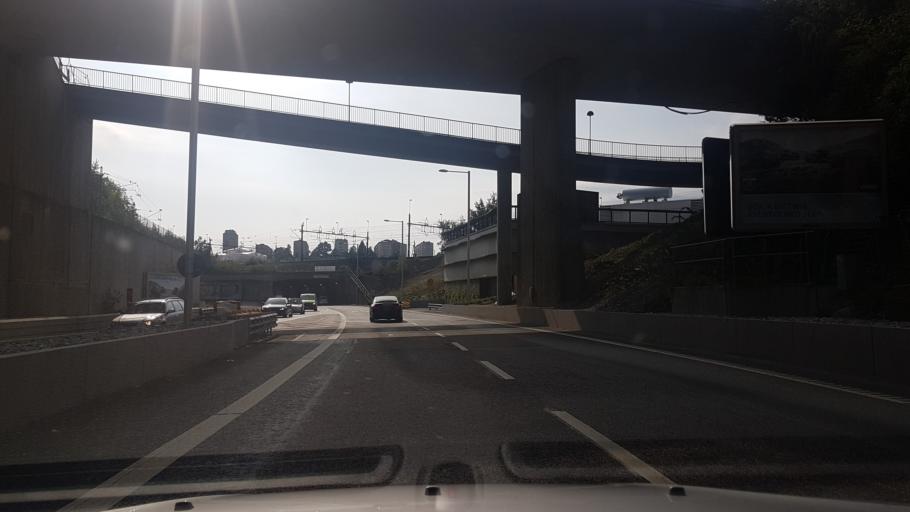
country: SE
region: Stockholm
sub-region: Solna Kommun
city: Solna
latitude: 59.3437
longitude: 18.0259
